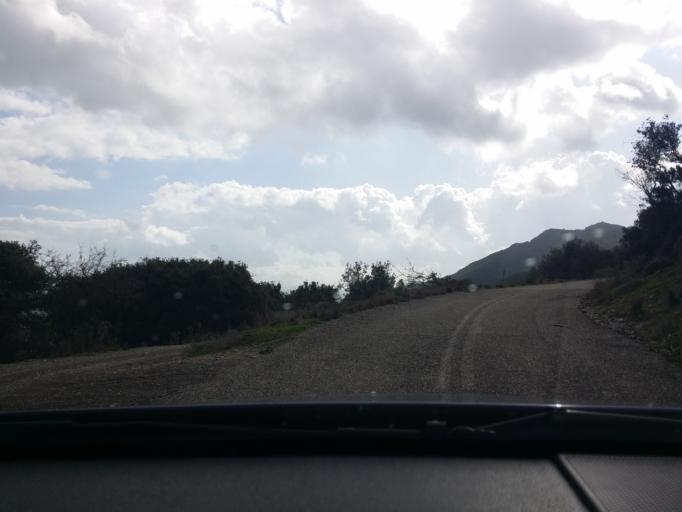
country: GR
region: West Greece
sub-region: Nomos Aitolias kai Akarnanias
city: Fitiai
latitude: 38.6739
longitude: 21.1914
